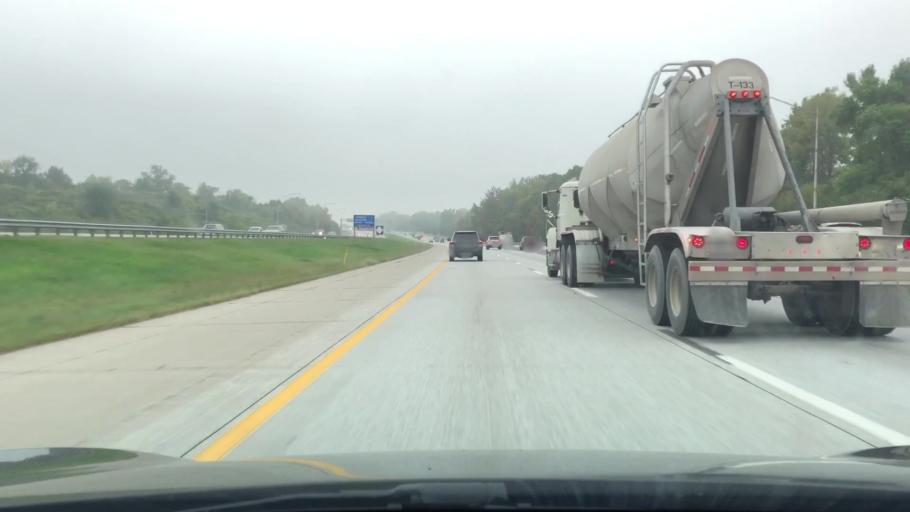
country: US
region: Pennsylvania
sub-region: Montgomery County
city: Conshohocken
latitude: 40.0972
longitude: -75.3020
